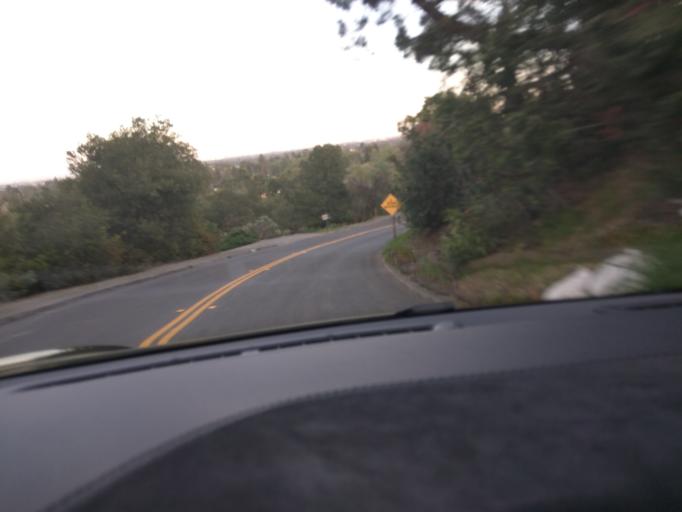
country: US
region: California
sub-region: Santa Clara County
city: Los Altos Hills
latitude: 37.3800
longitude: -122.1409
